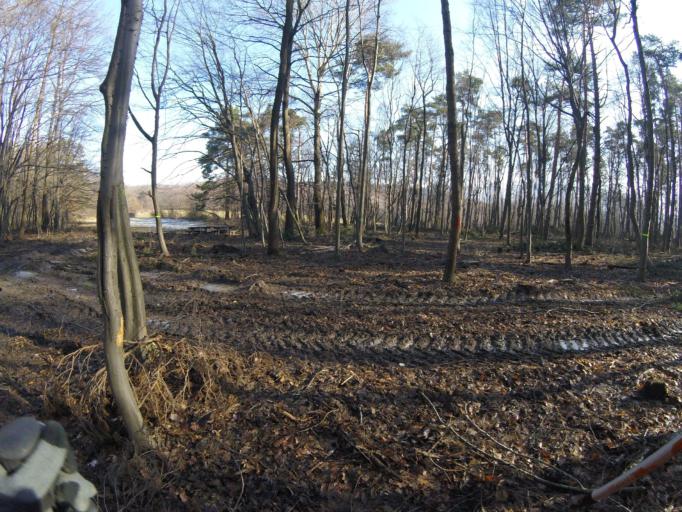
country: HU
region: Komarom-Esztergom
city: Pilismarot
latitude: 47.7479
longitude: 18.8839
